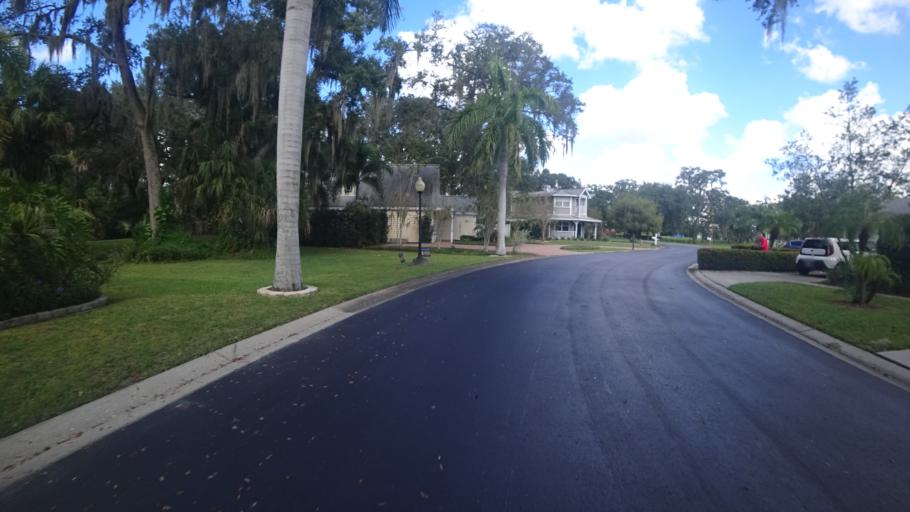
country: US
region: Florida
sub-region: Manatee County
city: Ellenton
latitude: 27.5328
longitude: -82.4942
